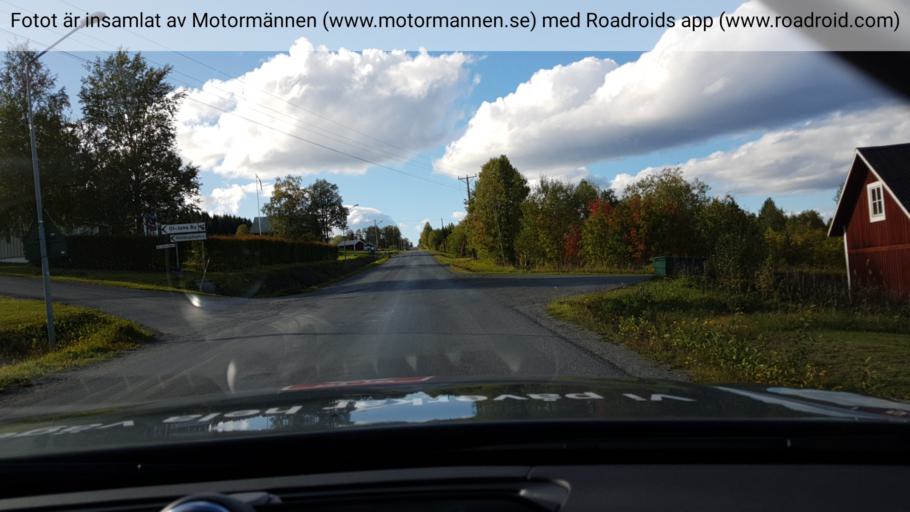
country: SE
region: Jaemtland
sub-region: Krokoms Kommun
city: Krokom
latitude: 63.1799
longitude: 14.0798
